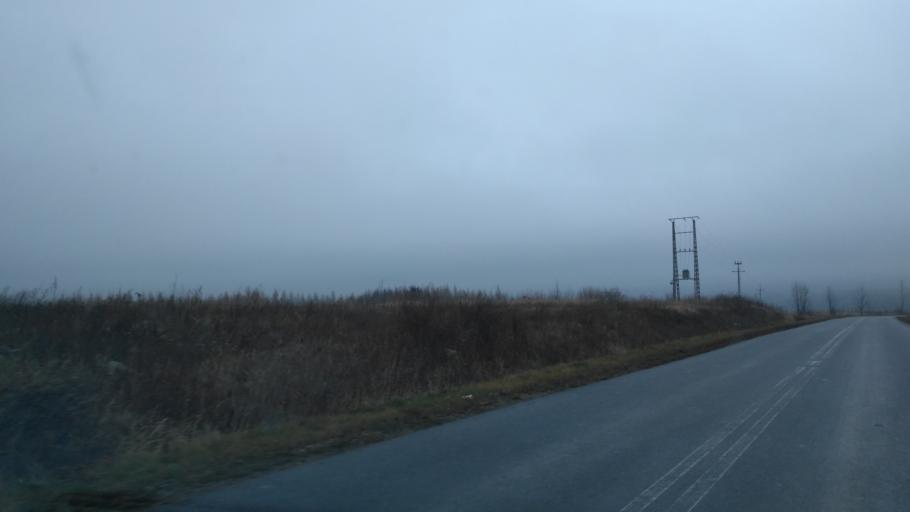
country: PL
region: Subcarpathian Voivodeship
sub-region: Powiat jaroslawski
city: Jodlowka
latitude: 49.9020
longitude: 22.4871
